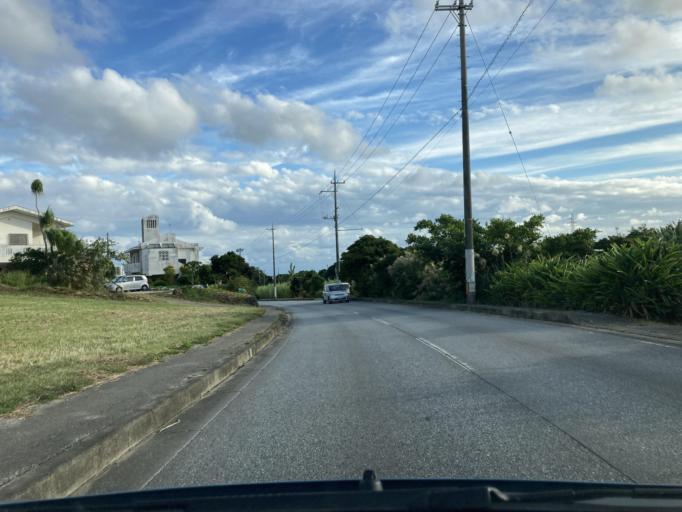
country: JP
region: Okinawa
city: Tomigusuku
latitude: 26.1452
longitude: 127.7453
